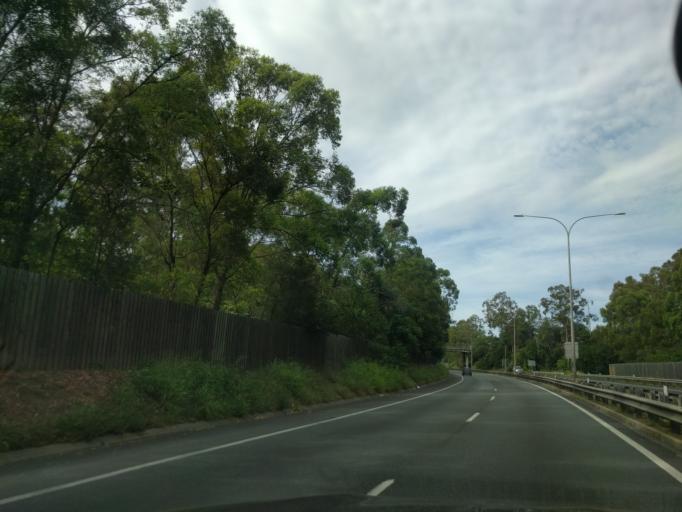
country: AU
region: Queensland
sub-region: Brisbane
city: Taringa
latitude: -27.5093
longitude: 152.9596
